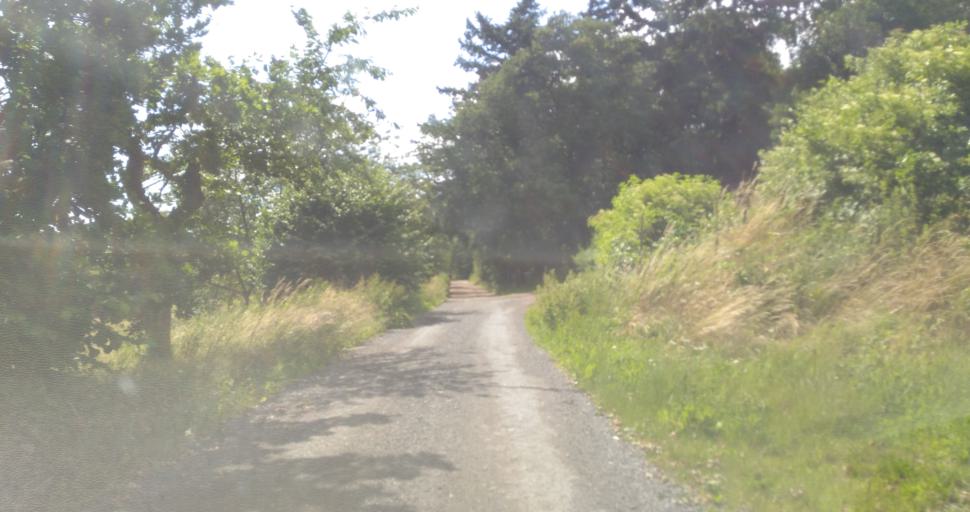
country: CZ
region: Plzensky
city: Zbiroh
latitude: 49.8571
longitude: 13.7509
